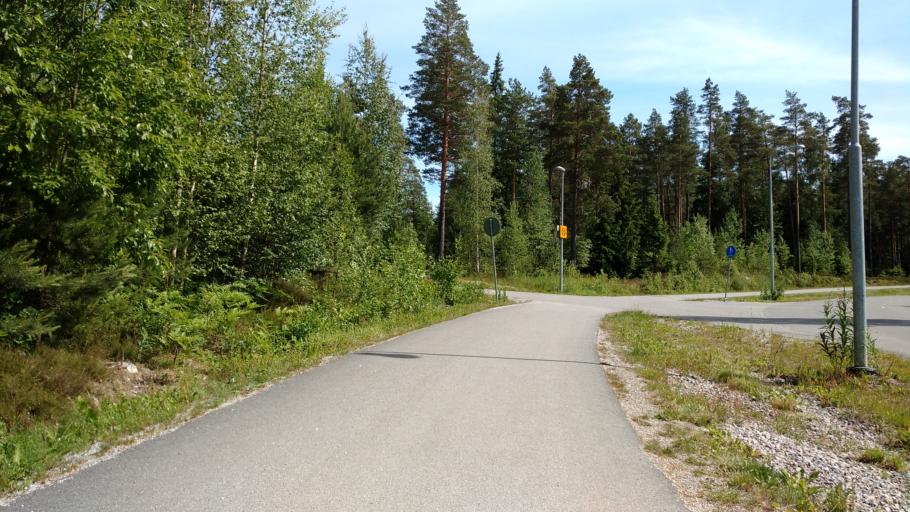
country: FI
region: Varsinais-Suomi
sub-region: Salo
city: Salo
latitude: 60.4013
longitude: 23.1909
